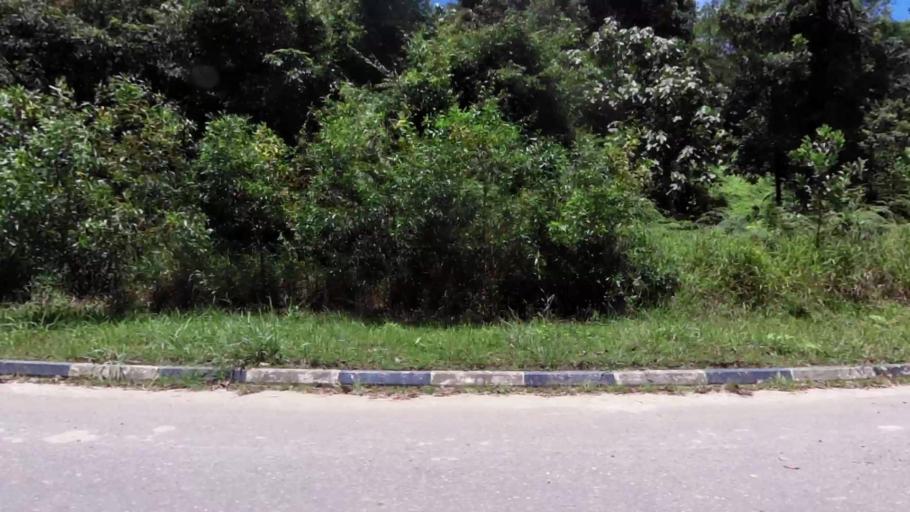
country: BN
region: Brunei and Muara
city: Bandar Seri Begawan
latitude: 4.9233
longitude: 114.9614
